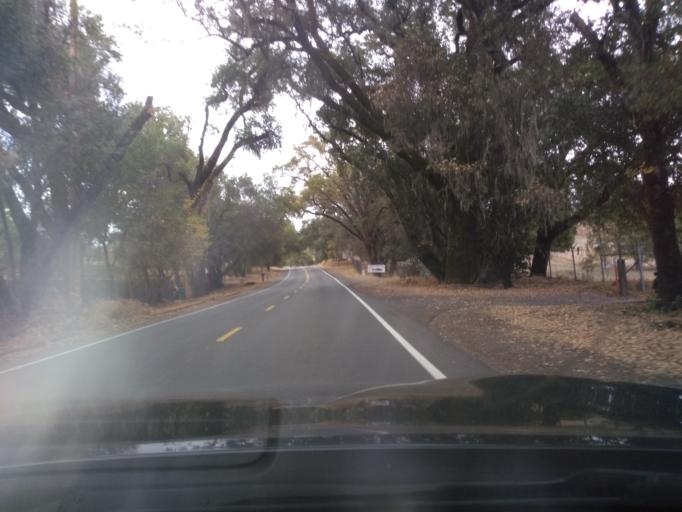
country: US
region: California
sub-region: Mendocino County
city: Ukiah
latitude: 39.1981
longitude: -123.1885
